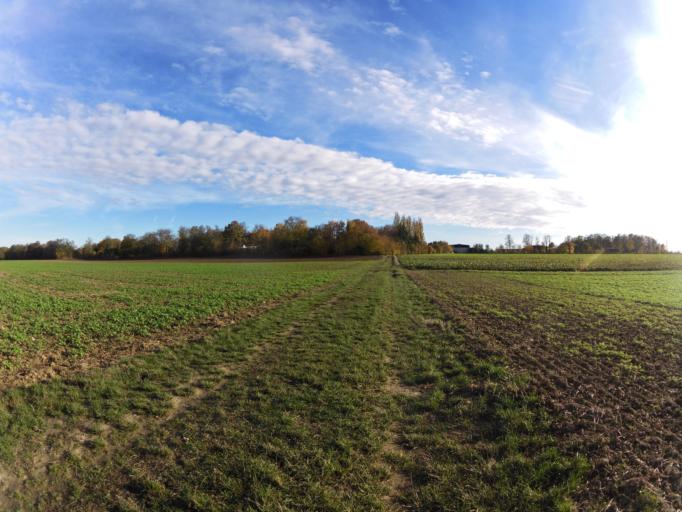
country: DE
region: Bavaria
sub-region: Regierungsbezirk Unterfranken
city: Giebelstadt
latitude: 49.6583
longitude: 9.9662
